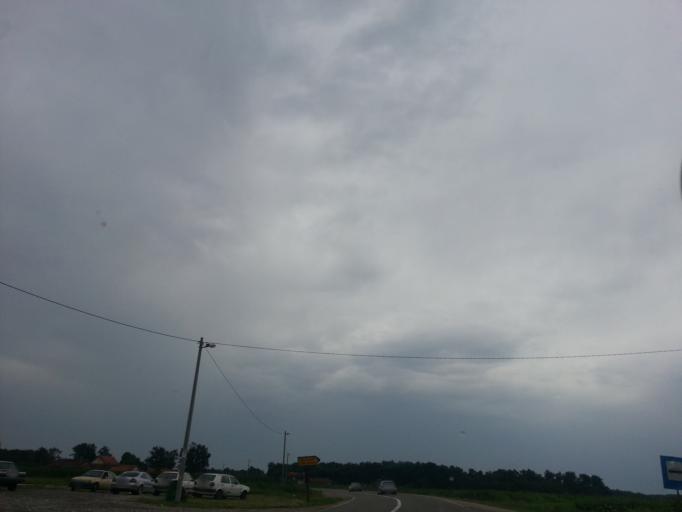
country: BA
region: Republika Srpska
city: Velika Obarska
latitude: 44.8227
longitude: 19.0441
